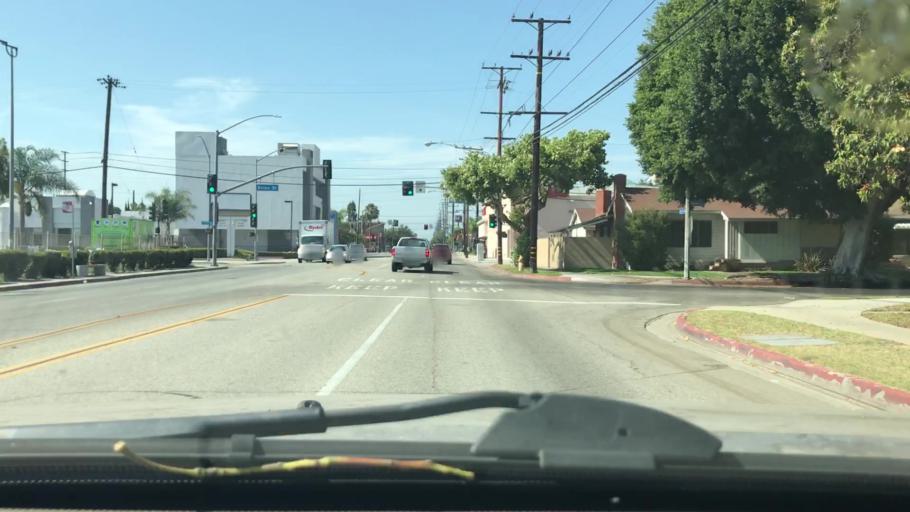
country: US
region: California
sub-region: Orange County
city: Rossmoor
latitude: 33.8086
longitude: -118.1078
